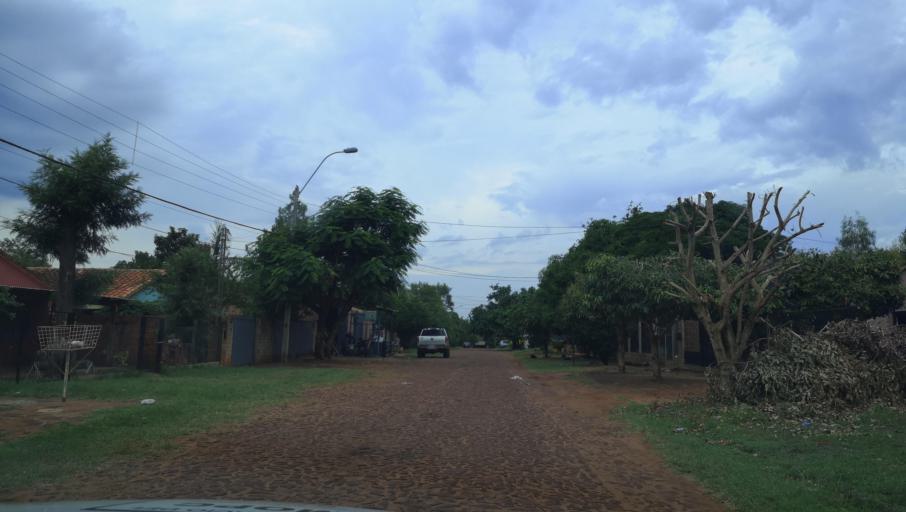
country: PY
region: Misiones
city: Santa Maria
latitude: -26.8878
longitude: -57.0434
